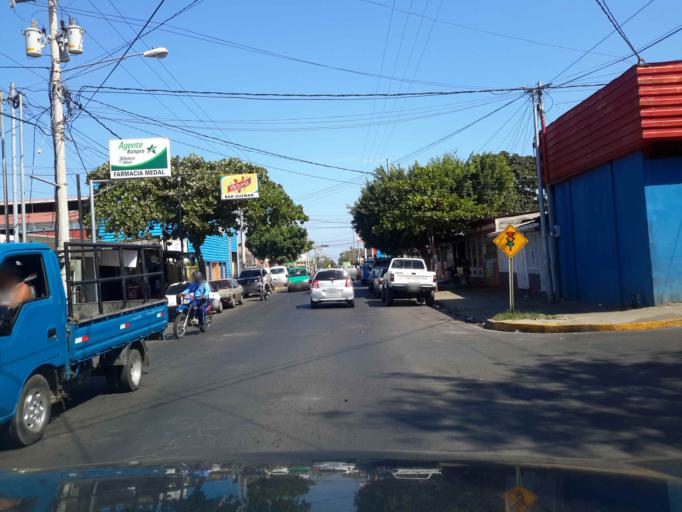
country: NI
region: Managua
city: Managua
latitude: 12.1524
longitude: -86.2889
